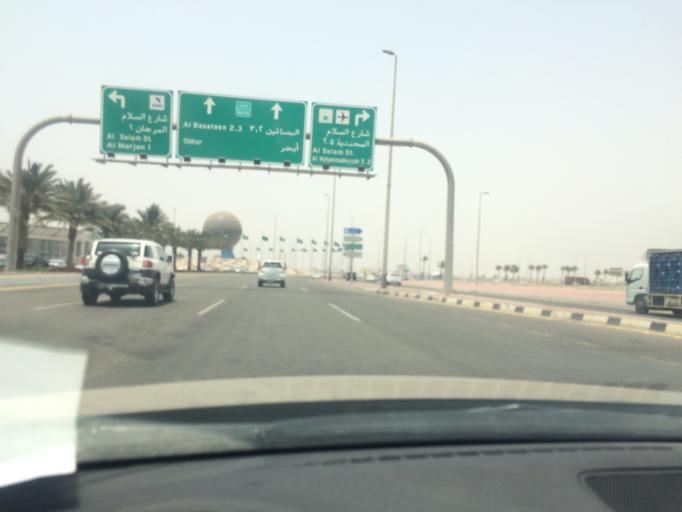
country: SA
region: Makkah
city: Jeddah
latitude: 21.6624
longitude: 39.1110
